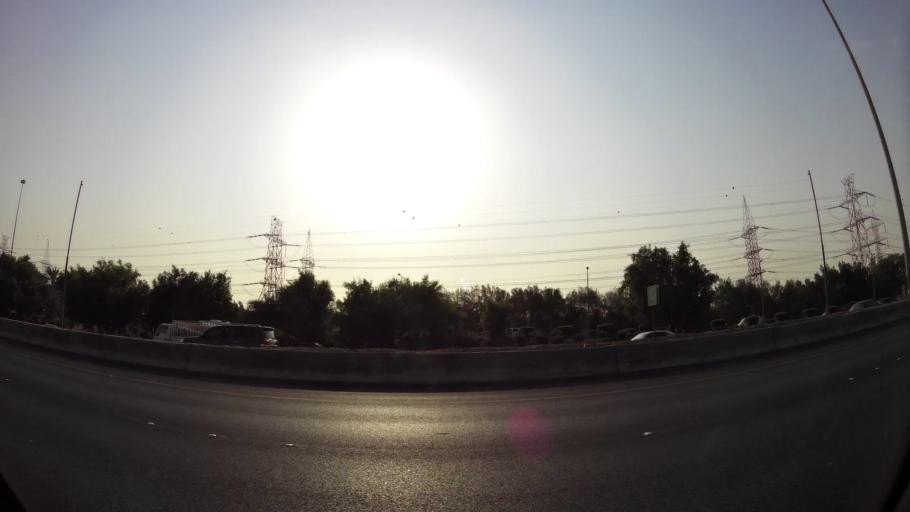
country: KW
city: Bayan
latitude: 29.2816
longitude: 48.0342
